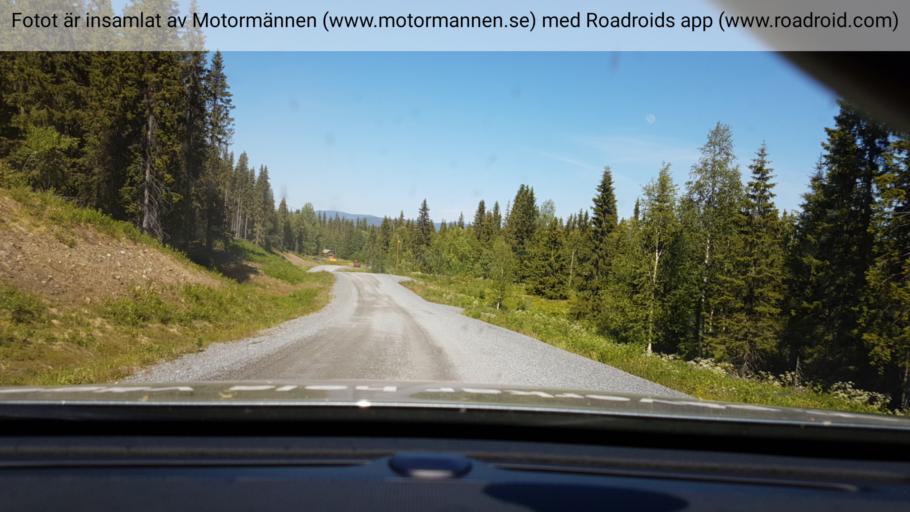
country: SE
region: Vaesterbotten
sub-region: Vilhelmina Kommun
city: Sjoberg
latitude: 64.7857
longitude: 15.9782
